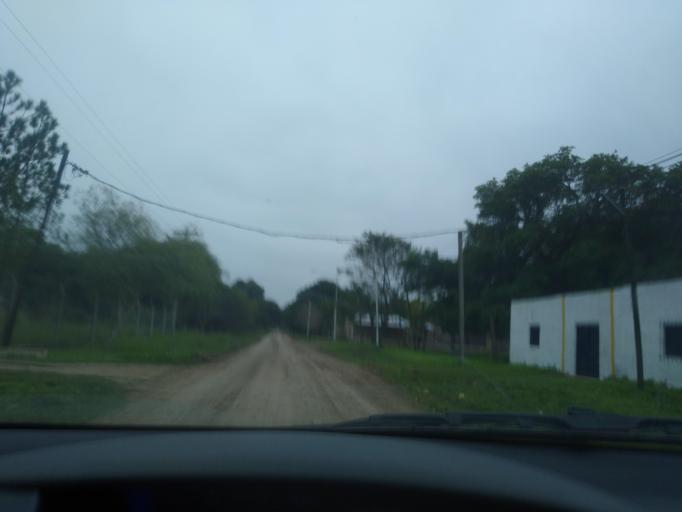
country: AR
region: Chaco
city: Colonia Benitez
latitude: -27.3328
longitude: -58.9609
